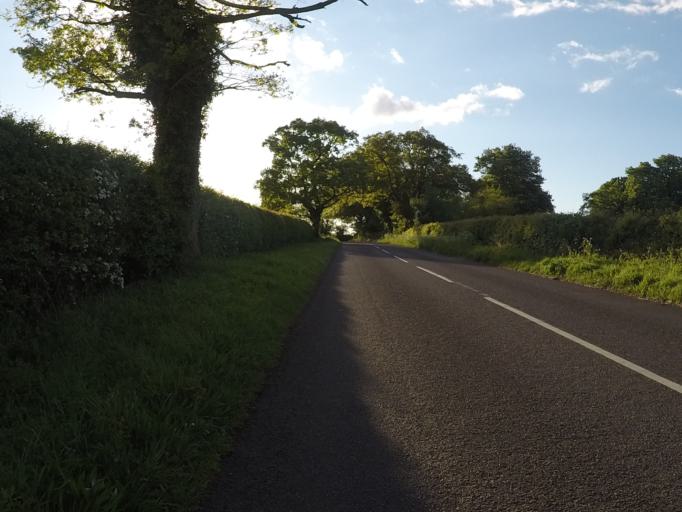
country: GB
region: England
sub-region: Oxfordshire
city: Charlbury
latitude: 51.8669
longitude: -1.4574
